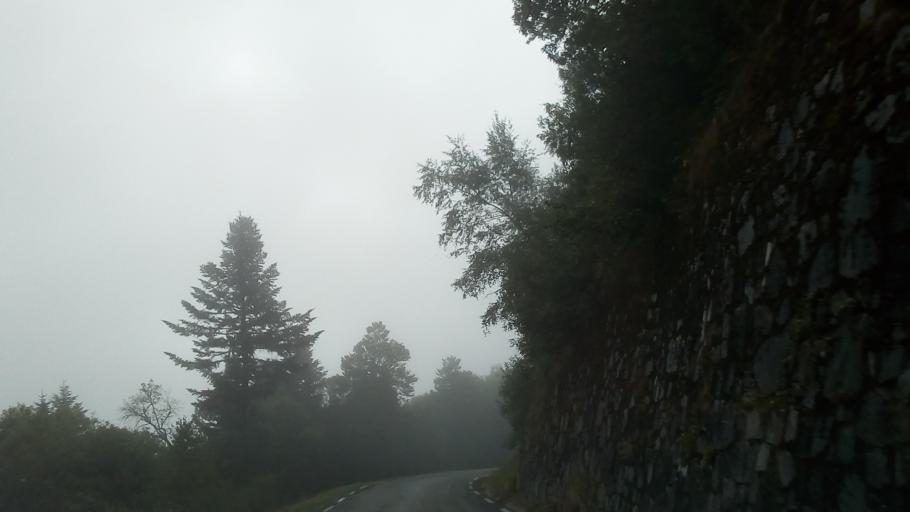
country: FR
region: Midi-Pyrenees
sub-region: Departement des Hautes-Pyrenees
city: Saint-Lary-Soulan
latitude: 42.7854
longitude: 0.1753
